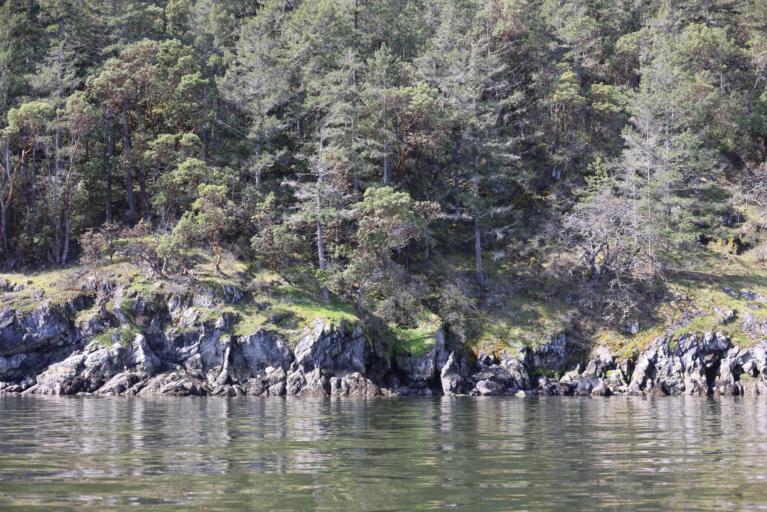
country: CA
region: British Columbia
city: Langford
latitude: 48.5750
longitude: -123.5160
